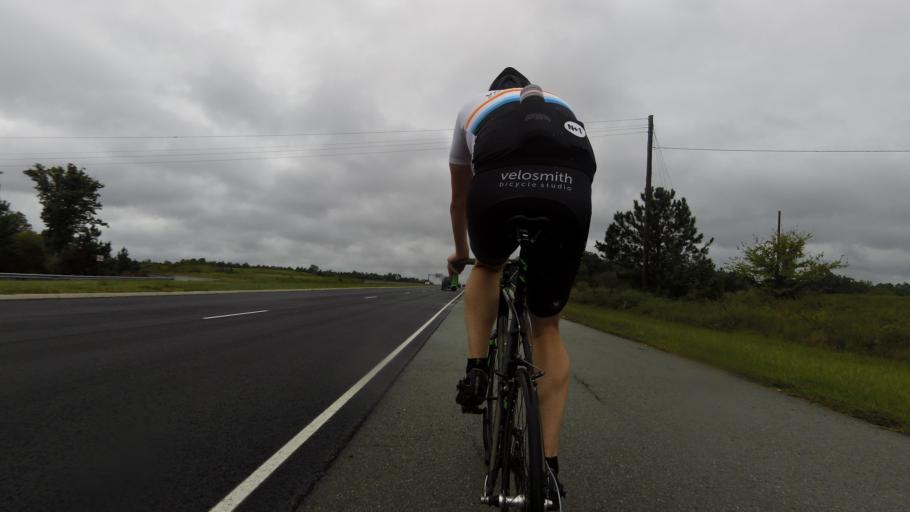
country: US
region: Virginia
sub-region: Henrico County
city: Short Pump
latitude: 37.5998
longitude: -77.6617
